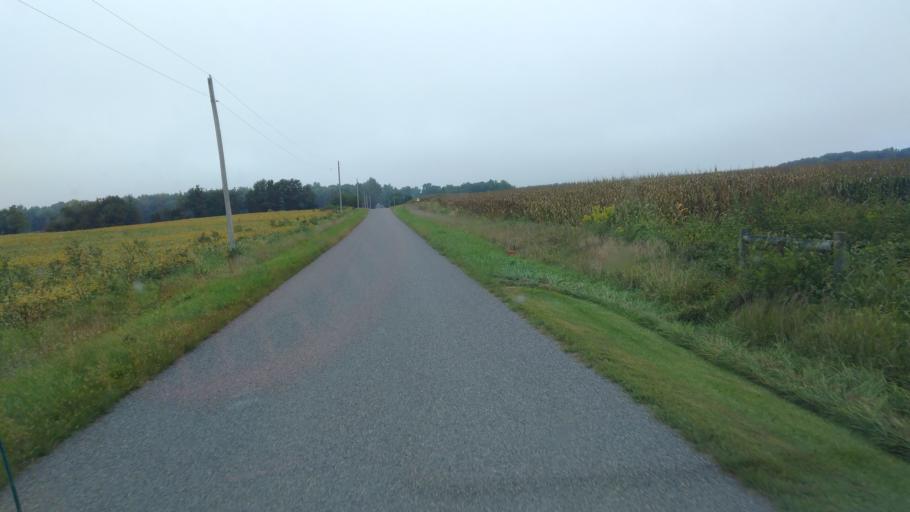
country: US
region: Ohio
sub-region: Logan County
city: Northwood
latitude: 40.4598
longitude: -83.5675
